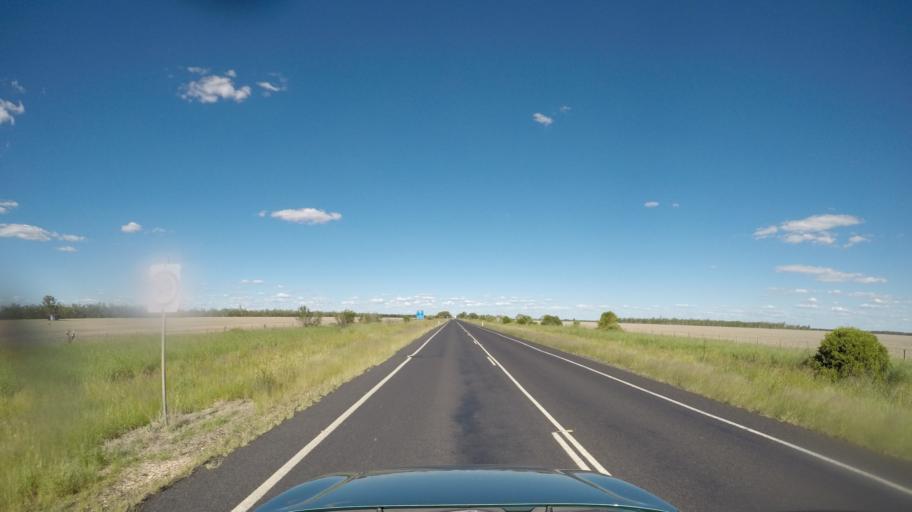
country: AU
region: Queensland
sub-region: Goondiwindi
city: Goondiwindi
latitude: -28.1774
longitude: 150.4742
